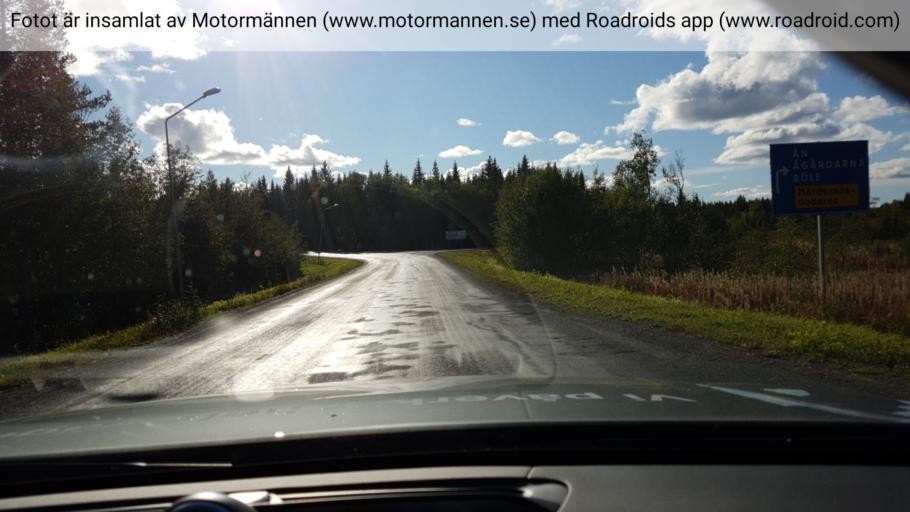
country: SE
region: Jaemtland
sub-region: Krokoms Kommun
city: Valla
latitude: 63.1842
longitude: 14.0173
